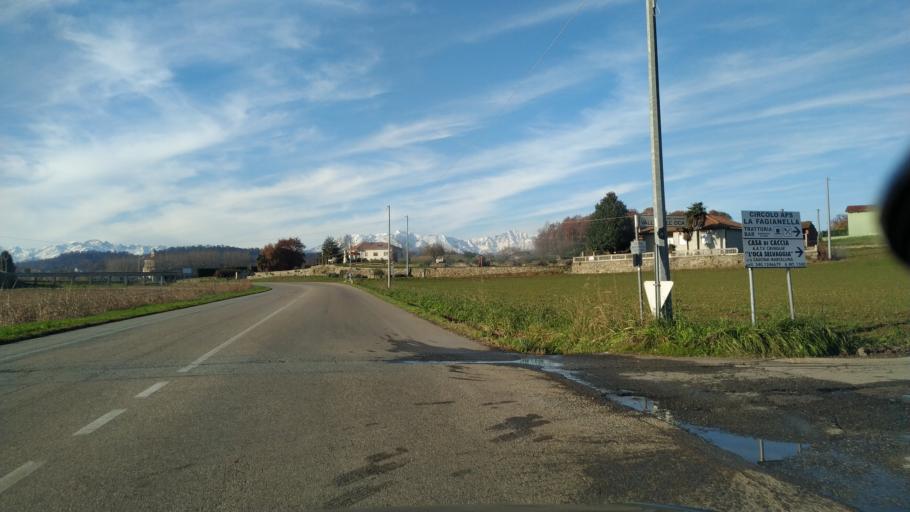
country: IT
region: Piedmont
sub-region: Provincia di Biella
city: Cavaglia
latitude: 45.4044
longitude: 8.1147
